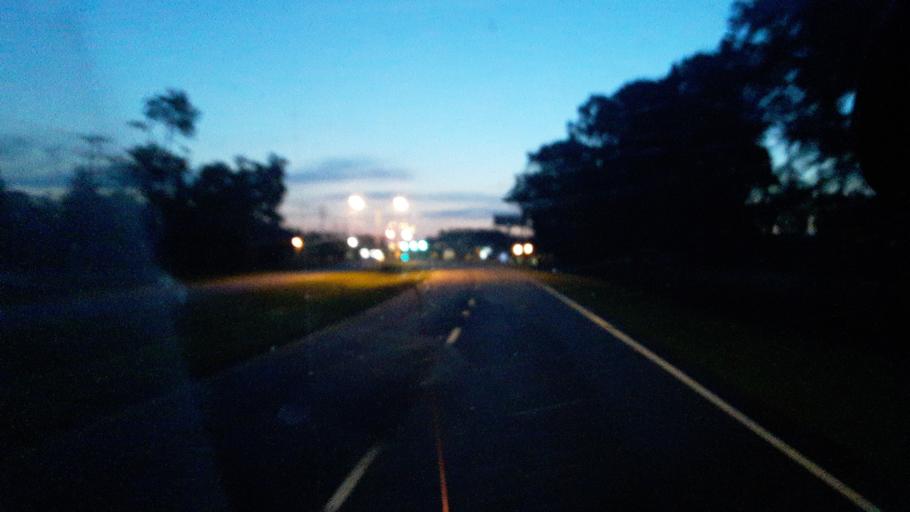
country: US
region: South Carolina
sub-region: Horry County
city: Little River
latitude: 33.8688
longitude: -78.6295
